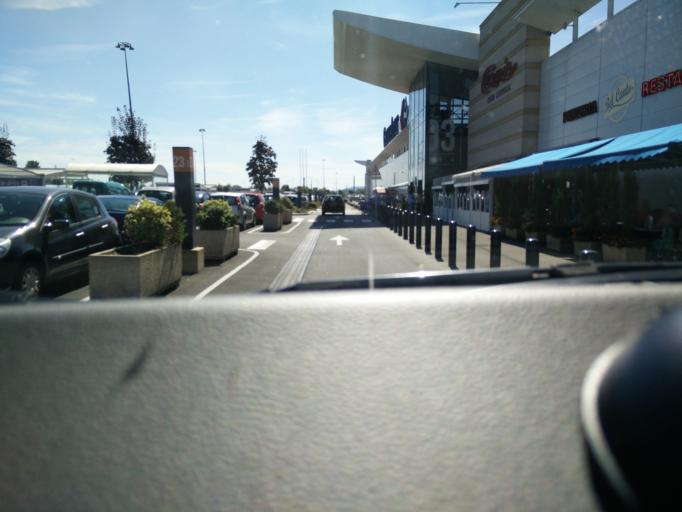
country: FR
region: Lorraine
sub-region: Departement de la Moselle
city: Terville
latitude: 49.3554
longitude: 6.1424
